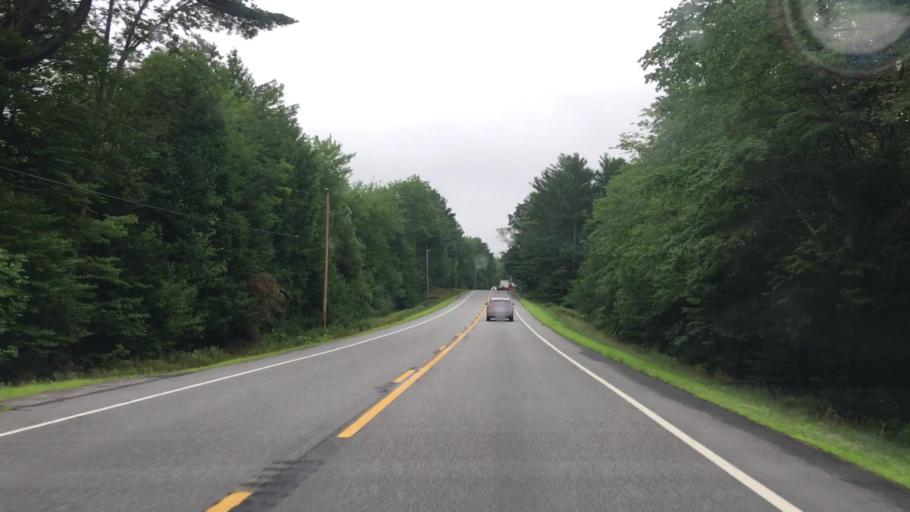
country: US
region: Maine
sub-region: Lincoln County
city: Jefferson
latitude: 44.2593
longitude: -69.4522
